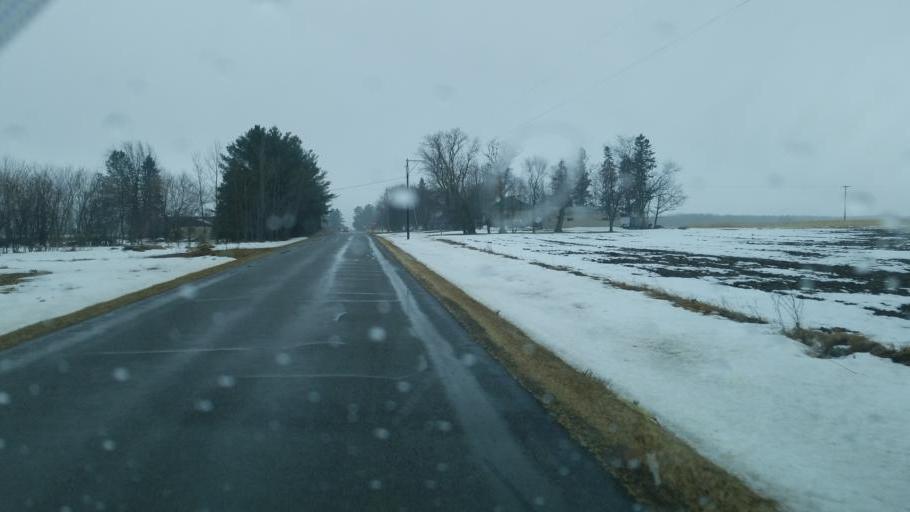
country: US
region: Wisconsin
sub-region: Marathon County
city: Spencer
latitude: 44.6582
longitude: -90.2792
